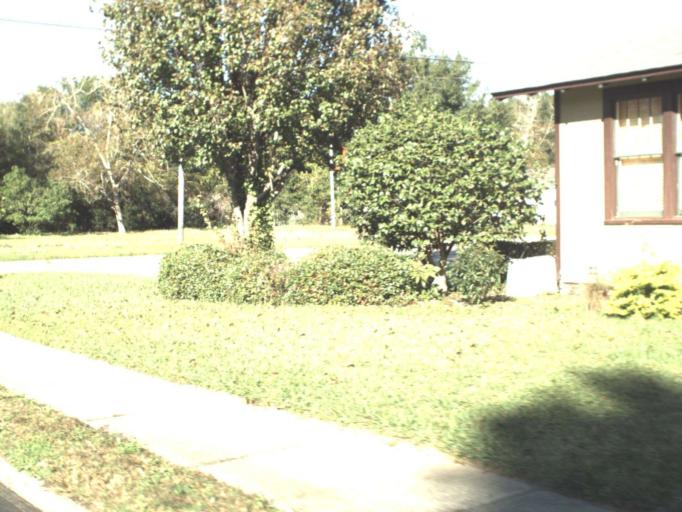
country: US
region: Florida
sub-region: Escambia County
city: Goulding
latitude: 30.4399
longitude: -87.2108
